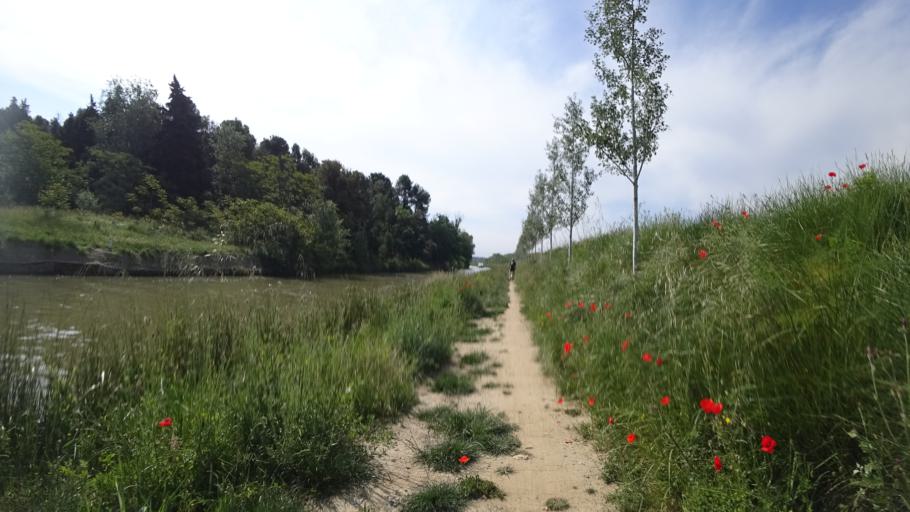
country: FR
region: Languedoc-Roussillon
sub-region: Departement de l'Herault
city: Olonzac
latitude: 43.2612
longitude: 2.7494
